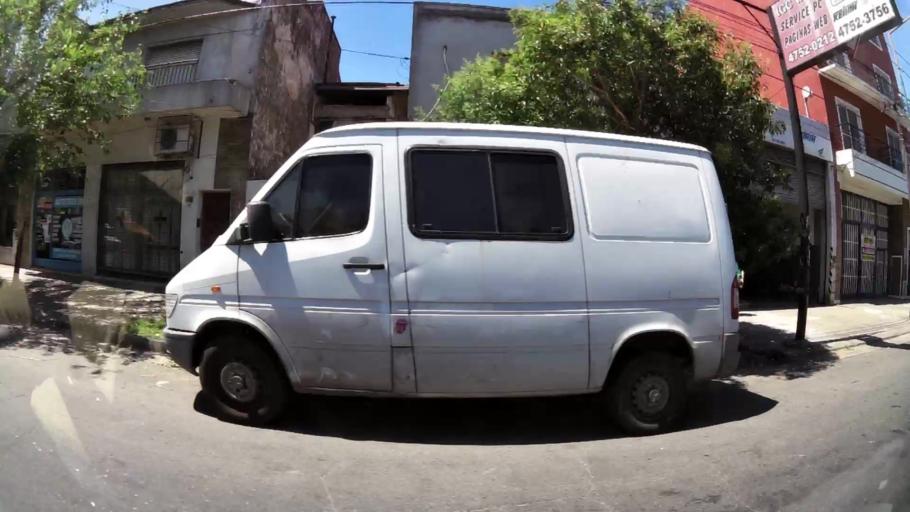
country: AR
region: Buenos Aires
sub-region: Partido de General San Martin
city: General San Martin
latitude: -34.5769
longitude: -58.5489
